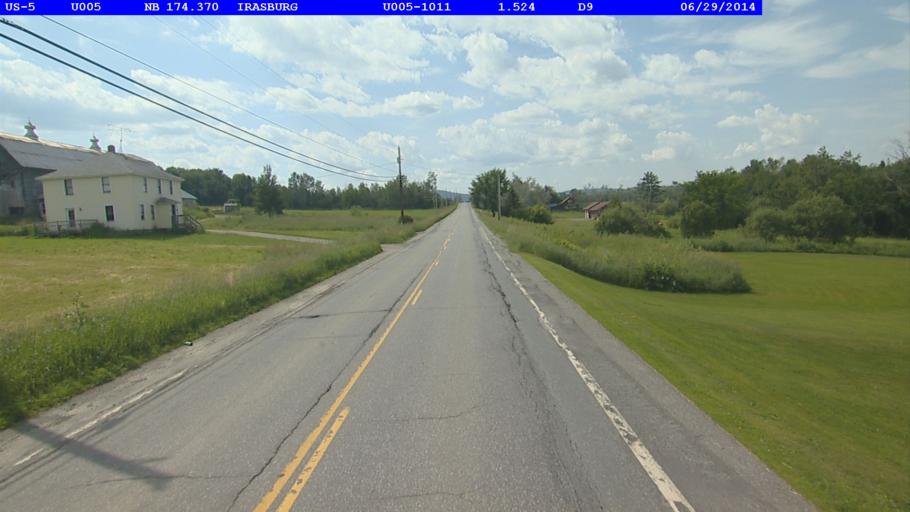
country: US
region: Vermont
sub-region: Orleans County
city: Newport
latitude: 44.8238
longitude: -72.2317
